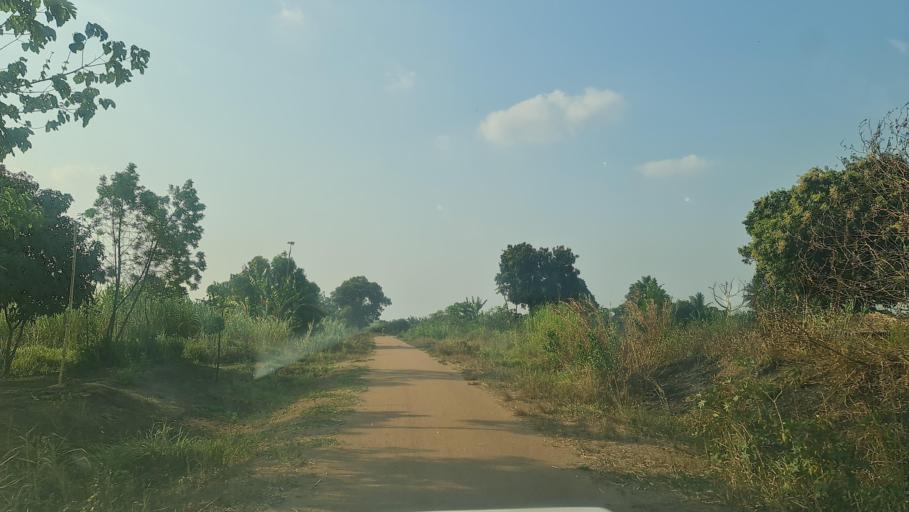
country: MZ
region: Zambezia
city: Quelimane
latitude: -18.1640
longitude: 35.9915
